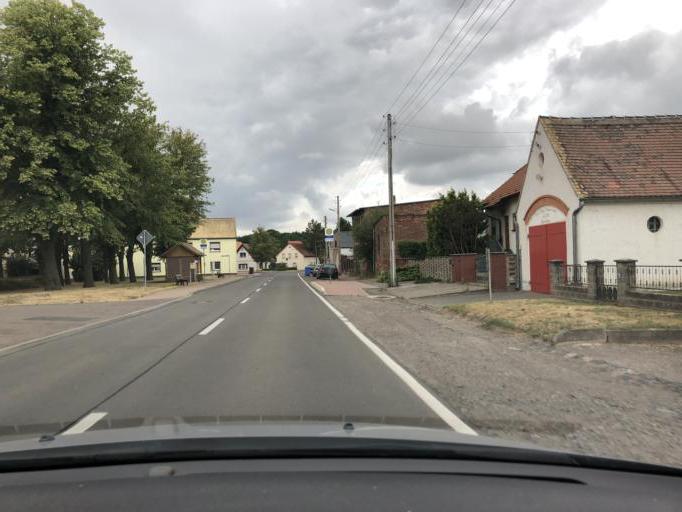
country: DE
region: Saxony-Anhalt
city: Ermlitz
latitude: 51.3873
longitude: 12.1448
